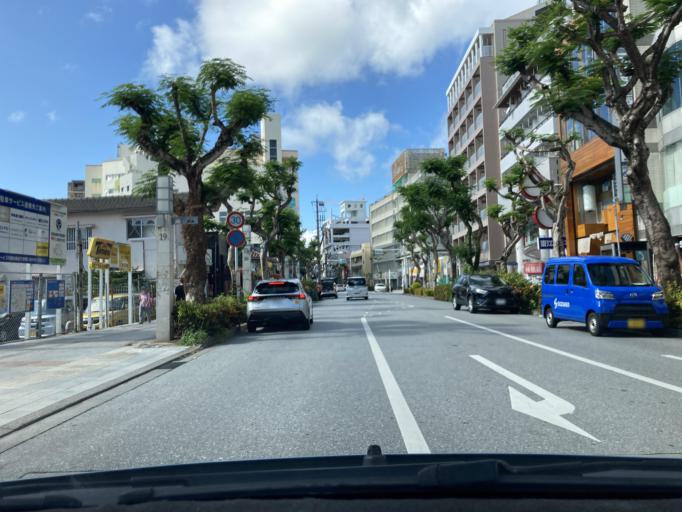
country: JP
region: Okinawa
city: Naha-shi
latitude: 26.2180
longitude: 127.6870
